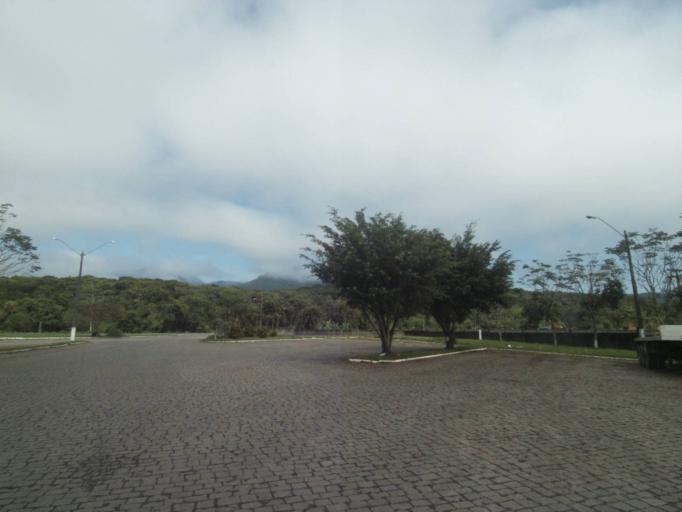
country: BR
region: Parana
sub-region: Paranagua
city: Paranagua
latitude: -25.5615
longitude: -48.6399
